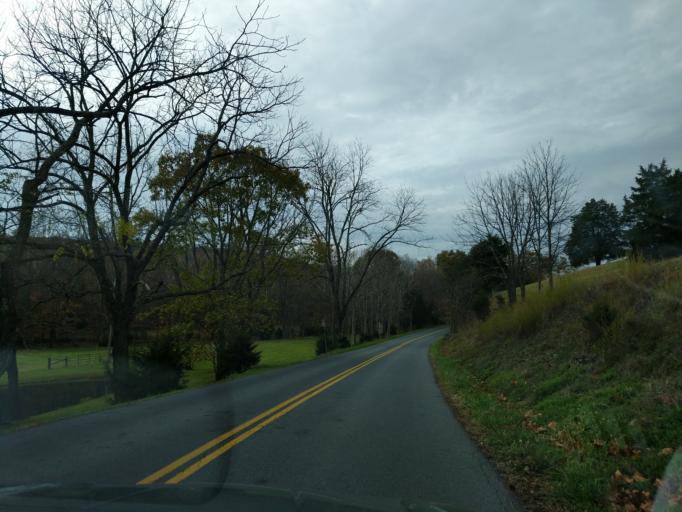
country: US
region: Virginia
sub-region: City of Winchester
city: Winchester
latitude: 39.3481
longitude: -78.2301
